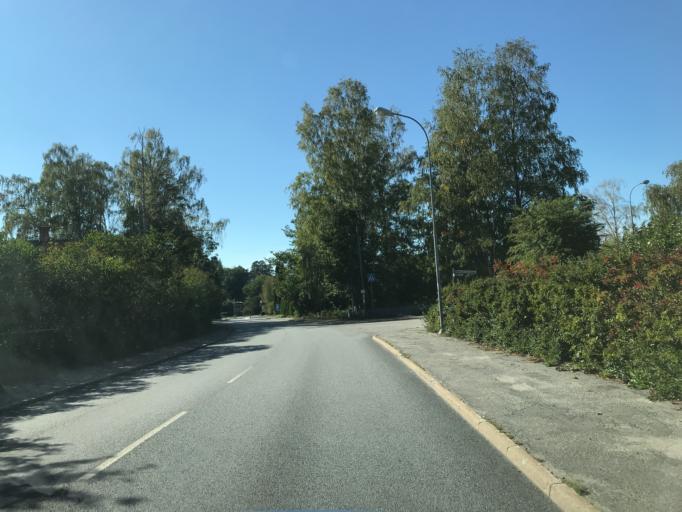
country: SE
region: Stockholm
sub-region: Sollentuna Kommun
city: Sollentuna
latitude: 59.4184
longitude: 17.9480
